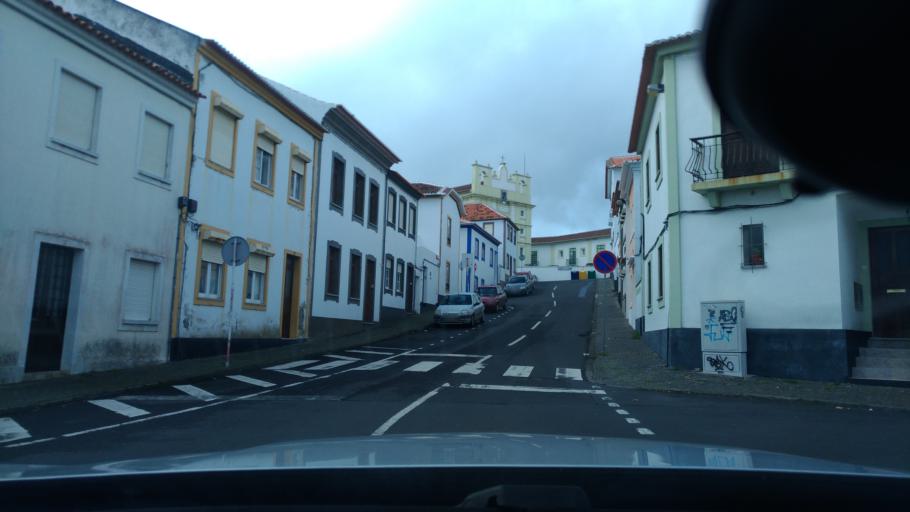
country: PT
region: Azores
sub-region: Angra do Heroismo
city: Angra do Heroismo
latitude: 38.6544
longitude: -27.2146
